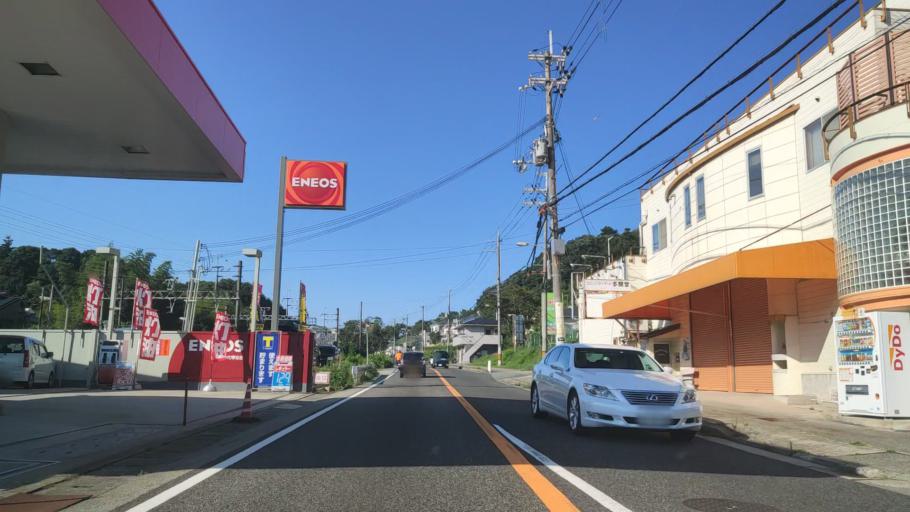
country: JP
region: Hyogo
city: Kobe
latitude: 34.7858
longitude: 135.2065
